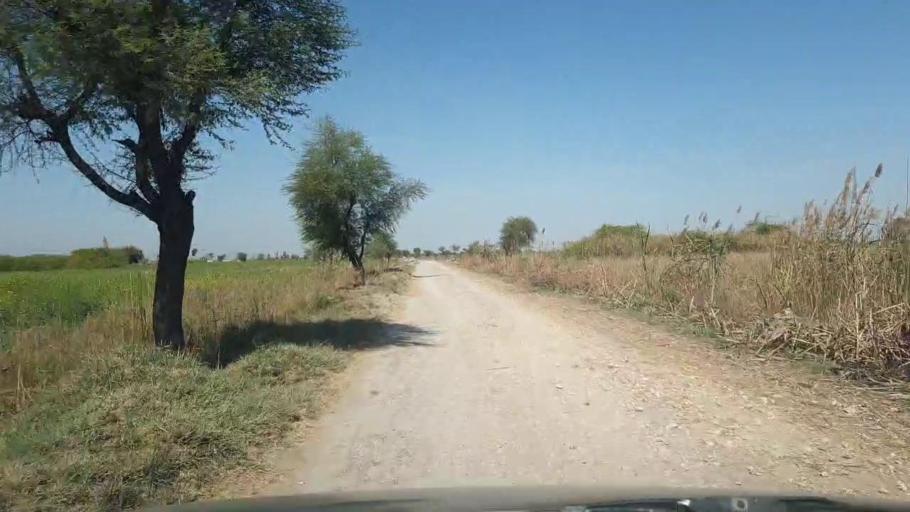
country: PK
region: Sindh
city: Dhoro Naro
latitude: 25.4411
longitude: 69.6170
